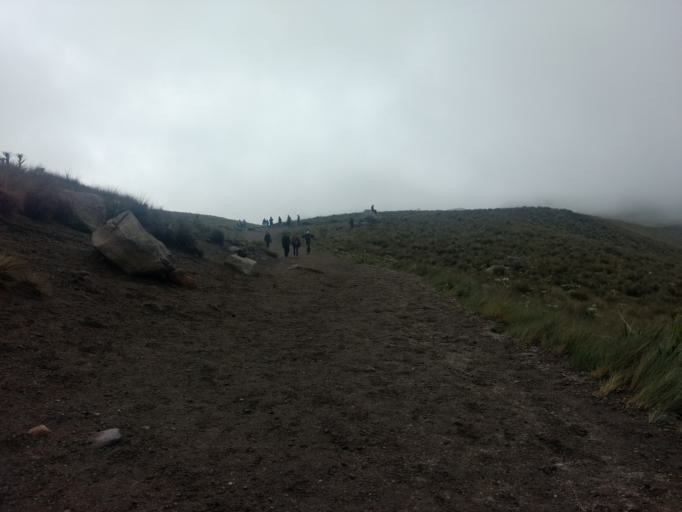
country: MX
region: Mexico
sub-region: Tenango del Valle
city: Santa Cruz Pueblo Nuevo (Pueblo Nuevo)
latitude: 19.1140
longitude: -99.7514
